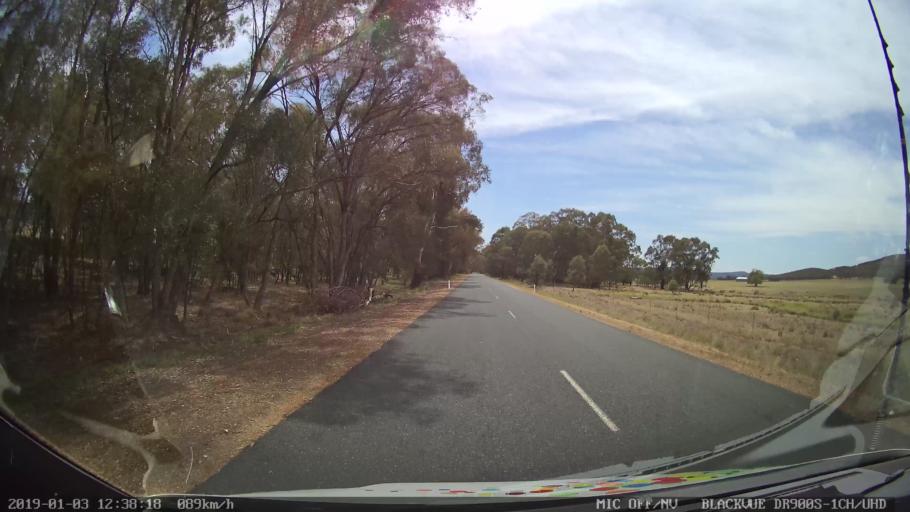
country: AU
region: New South Wales
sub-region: Weddin
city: Grenfell
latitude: -33.8344
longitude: 148.1938
